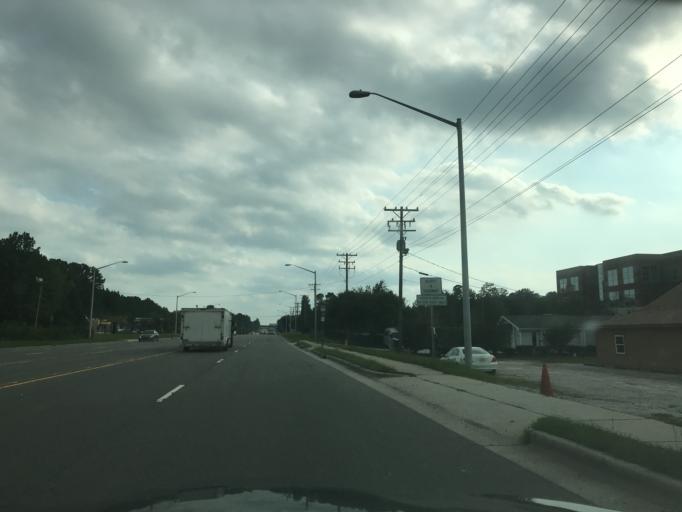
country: US
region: North Carolina
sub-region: Durham County
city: Durham
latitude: 35.9151
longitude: -78.8917
